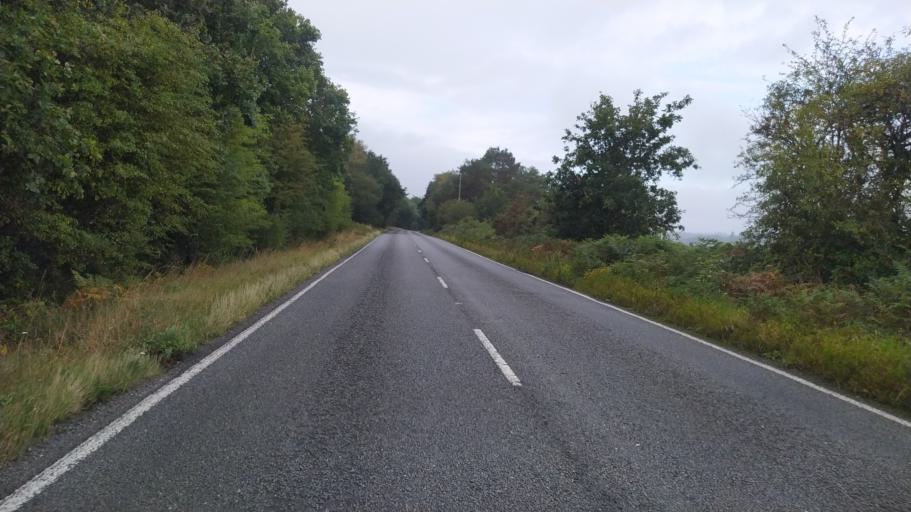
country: GB
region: England
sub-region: Hampshire
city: New Milton
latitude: 50.8108
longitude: -1.6641
